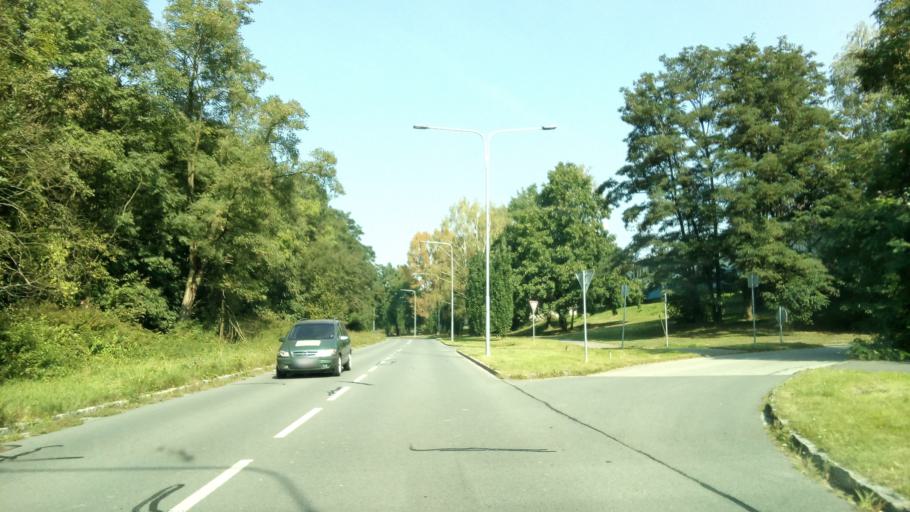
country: CZ
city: Vresina
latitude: 49.8329
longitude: 18.1577
